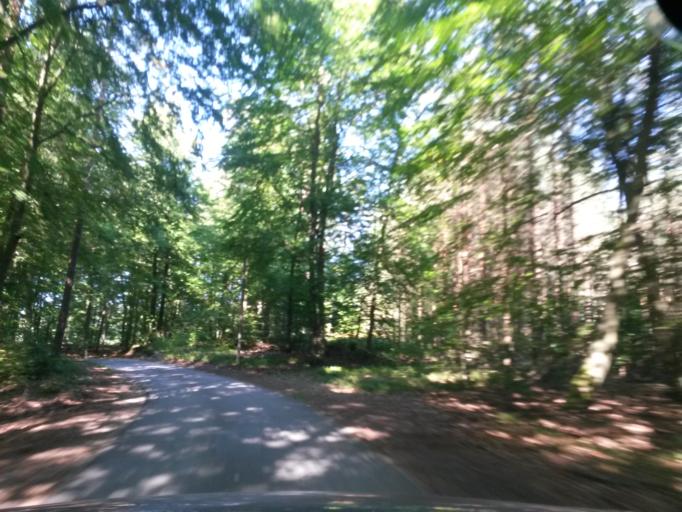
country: DE
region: Brandenburg
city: Lychen
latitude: 53.1798
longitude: 13.3523
